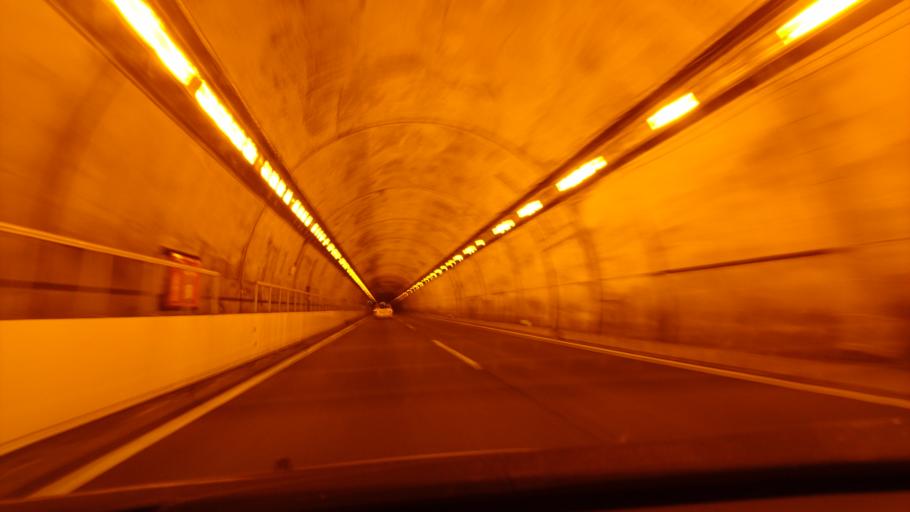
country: JP
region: Akita
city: Hanawa
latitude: 40.0193
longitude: 140.9851
